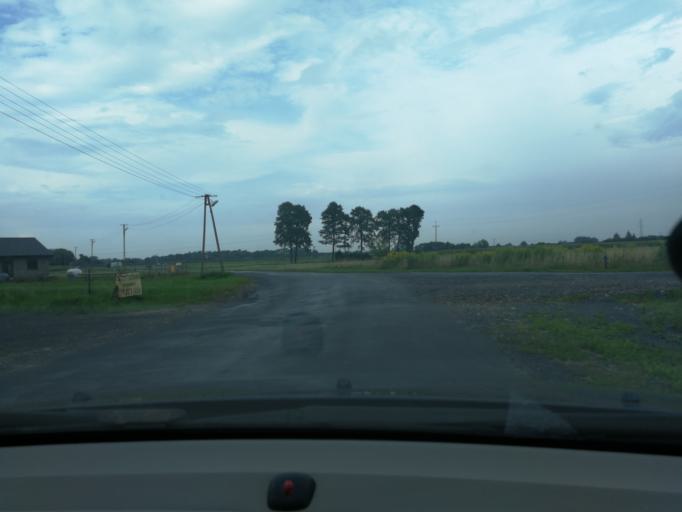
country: PL
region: Masovian Voivodeship
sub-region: Powiat grodziski
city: Grodzisk Mazowiecki
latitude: 52.1217
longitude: 20.5806
